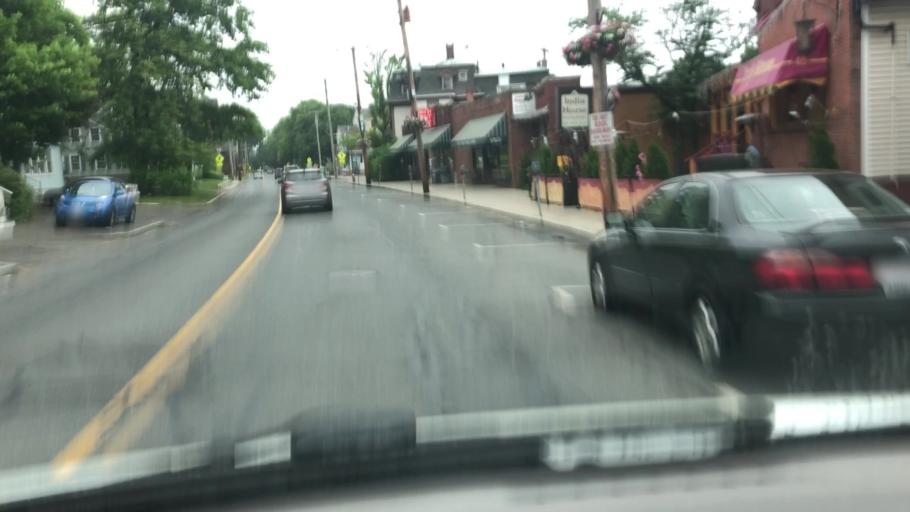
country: US
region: Massachusetts
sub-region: Hampshire County
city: Northampton
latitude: 42.3189
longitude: -72.6342
